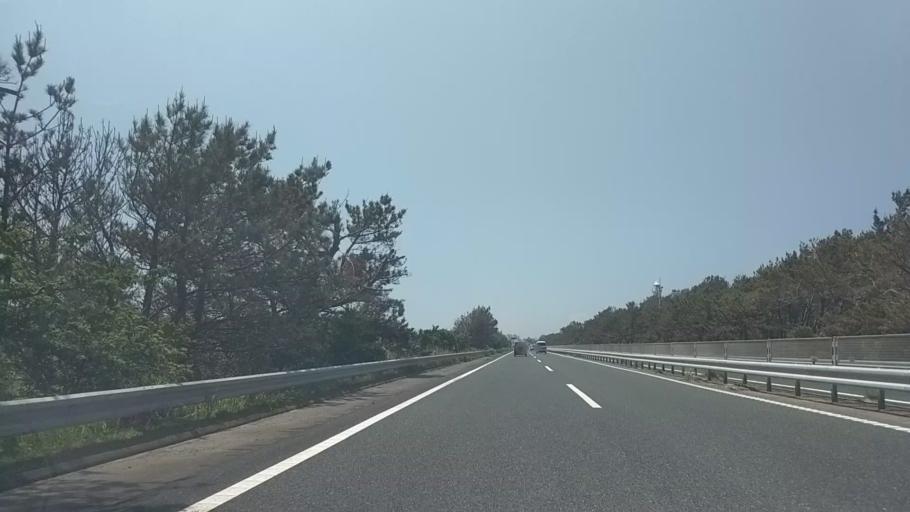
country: JP
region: Shizuoka
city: Kosai-shi
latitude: 34.6779
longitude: 137.6168
